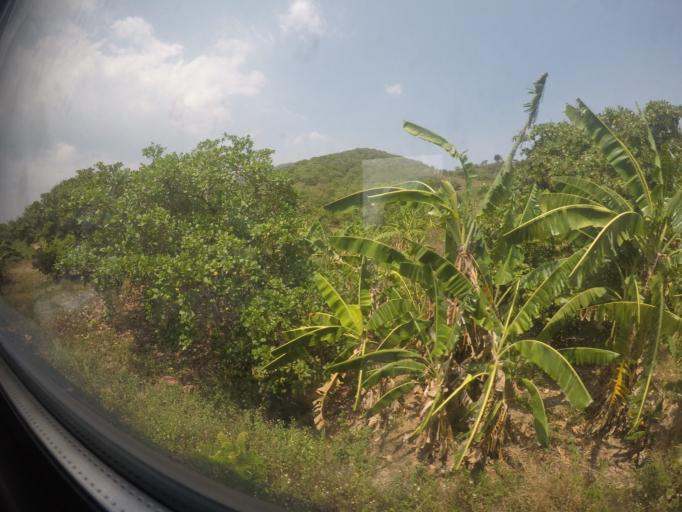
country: VN
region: Binh Thuan
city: Thuan Nam
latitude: 10.8816
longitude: 107.7066
